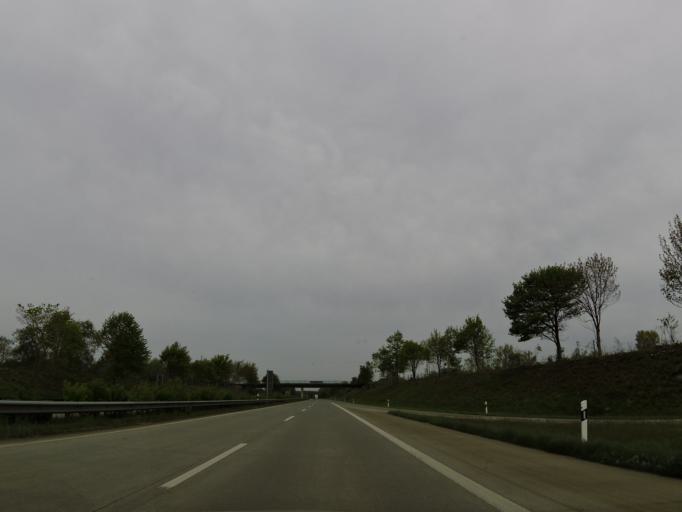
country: DE
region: Schleswig-Holstein
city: Neuenbrook
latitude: 53.8734
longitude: 9.5584
